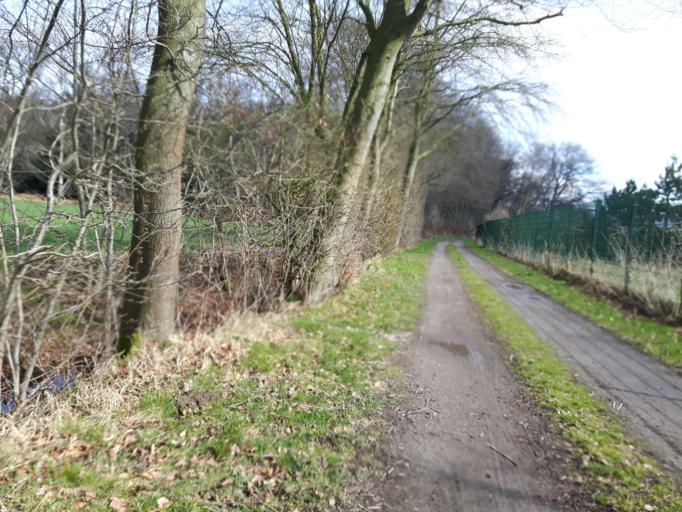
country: DE
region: North Rhine-Westphalia
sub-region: Regierungsbezirk Munster
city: Senden
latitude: 51.8688
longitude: 7.4880
